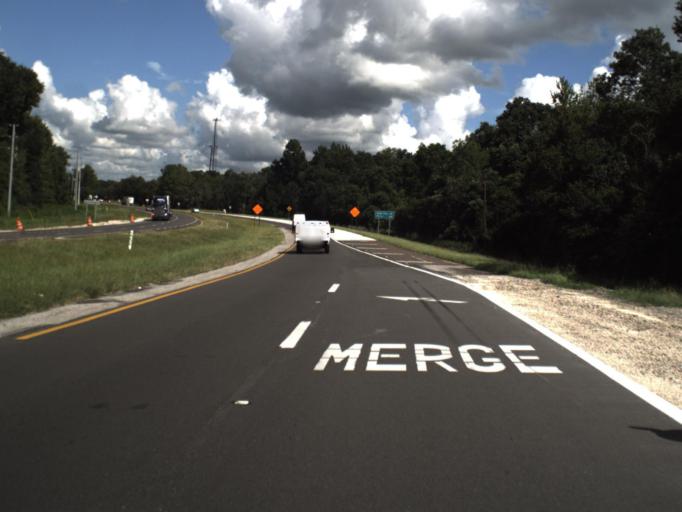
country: US
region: Florida
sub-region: Polk County
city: Gibsonia
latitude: 28.1651
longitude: -81.9746
